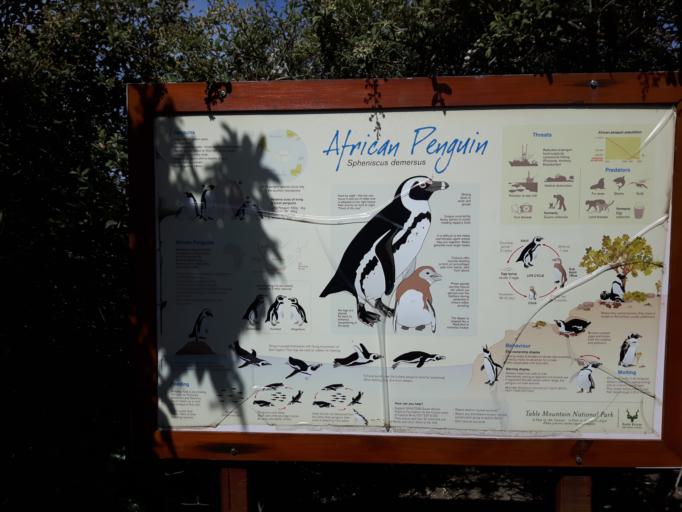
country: ZA
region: Western Cape
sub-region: City of Cape Town
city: Retreat
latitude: -34.1957
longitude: 18.4495
